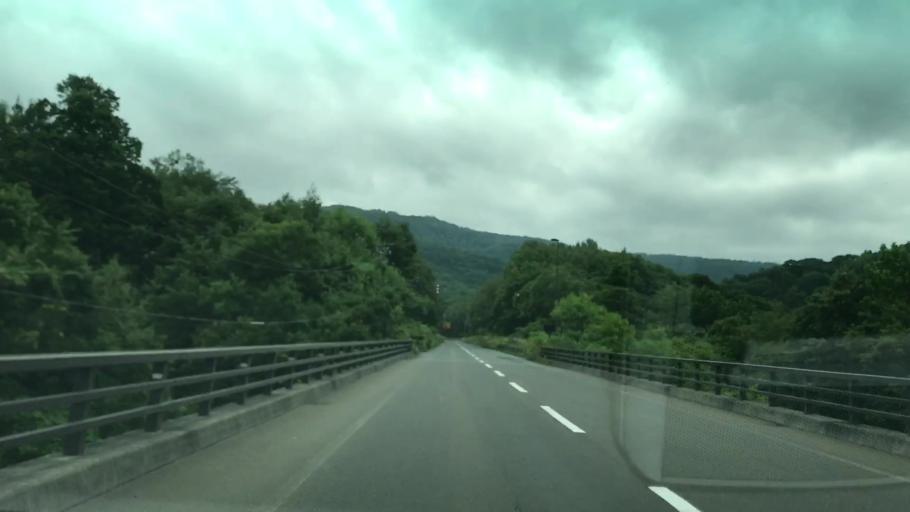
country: JP
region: Hokkaido
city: Yoichi
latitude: 43.0095
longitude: 140.8717
